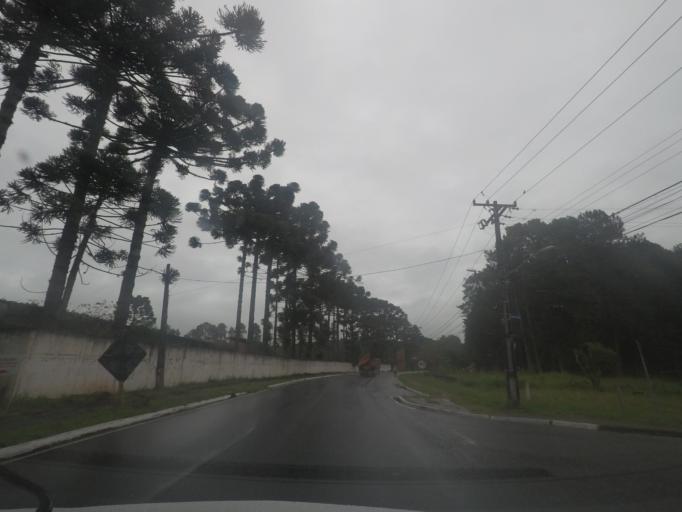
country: BR
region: Parana
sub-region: Quatro Barras
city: Quatro Barras
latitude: -25.3804
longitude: -49.1234
